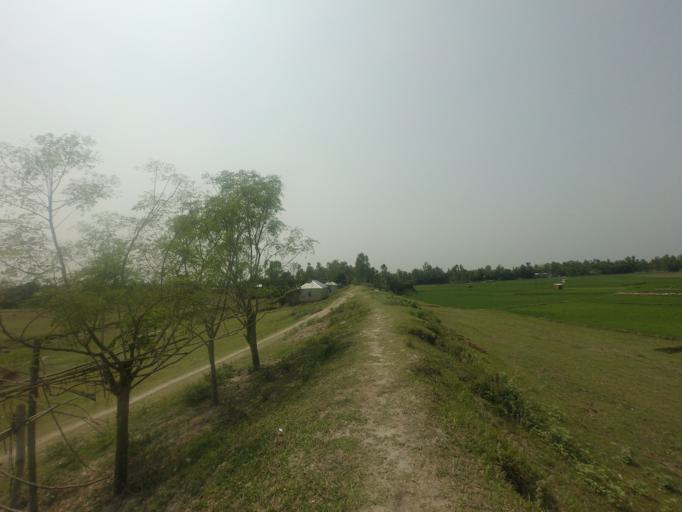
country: BD
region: Rajshahi
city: Sirajganj
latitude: 24.3535
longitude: 89.7237
